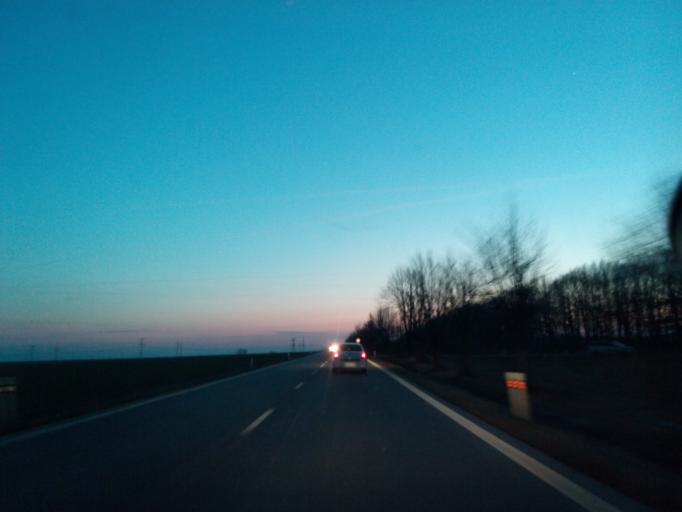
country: SK
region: Kosicky
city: Michalovce
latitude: 48.7179
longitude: 21.8440
